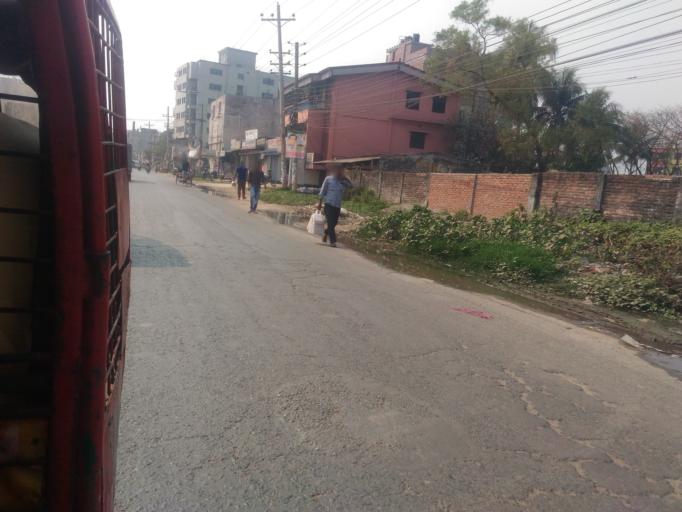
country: BD
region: Dhaka
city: Tungi
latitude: 23.9918
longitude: 90.3961
